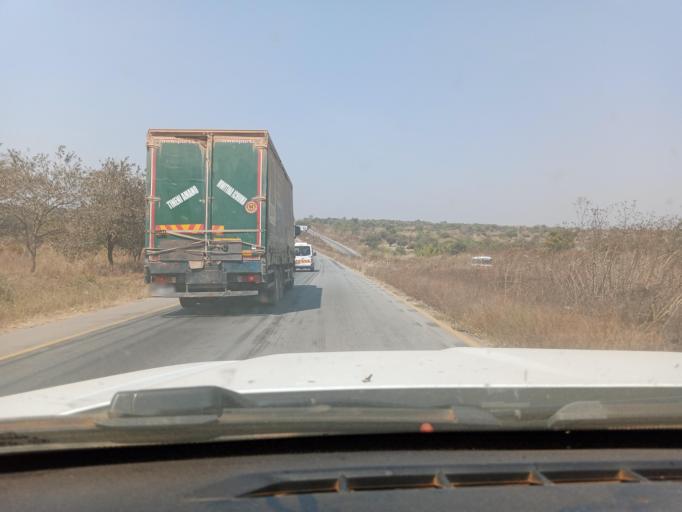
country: ZM
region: Copperbelt
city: Luanshya
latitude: -13.0156
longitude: 28.4356
